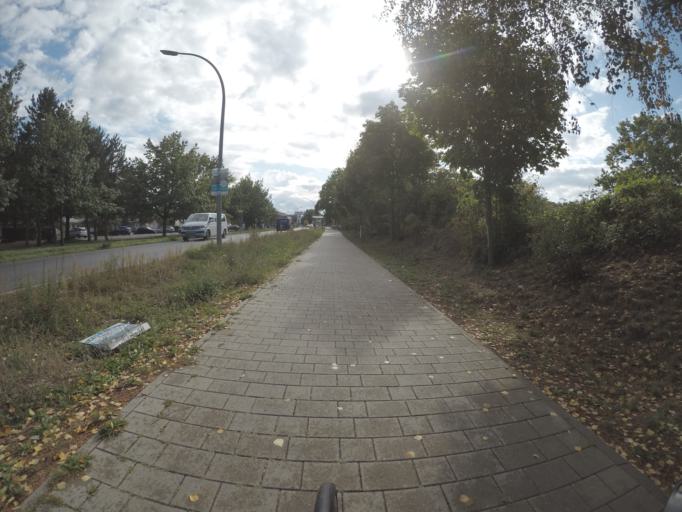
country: DE
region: Brandenburg
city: Strausberg
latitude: 52.5513
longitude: 13.8640
